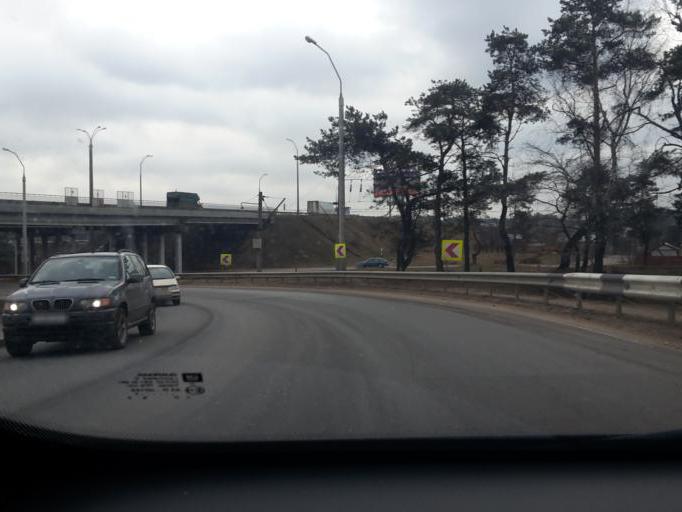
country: BY
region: Minsk
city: Vyaliki Trastsyanets
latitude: 53.9224
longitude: 27.6797
